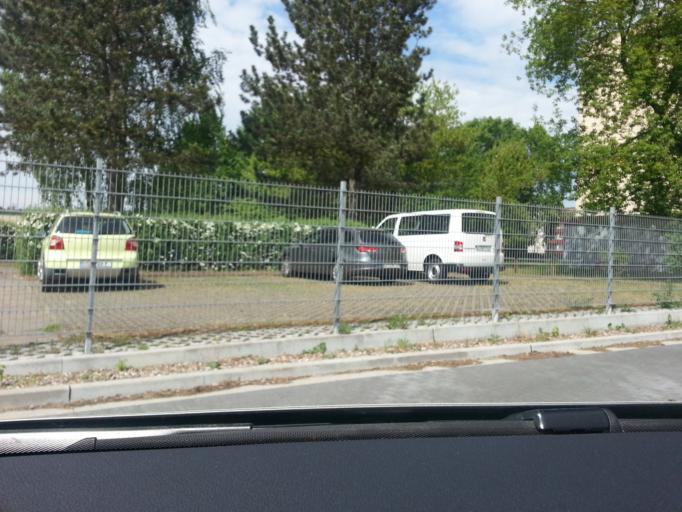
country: DE
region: Mecklenburg-Vorpommern
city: Torgelow
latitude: 53.6356
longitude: 14.0177
